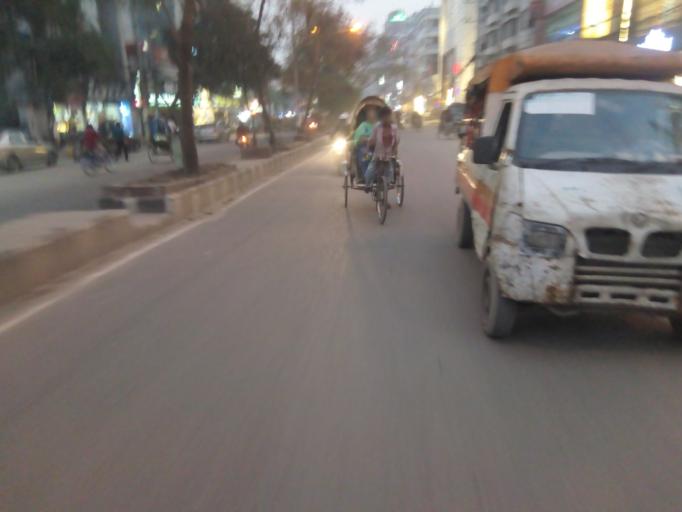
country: BD
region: Dhaka
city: Azimpur
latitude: 23.7681
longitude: 90.3584
